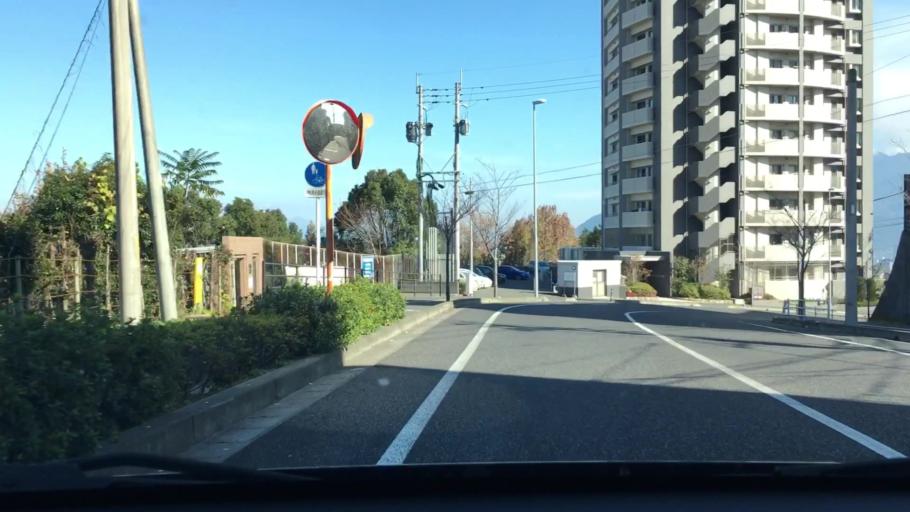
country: JP
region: Kagoshima
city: Kagoshima-shi
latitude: 31.5632
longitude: 130.5371
